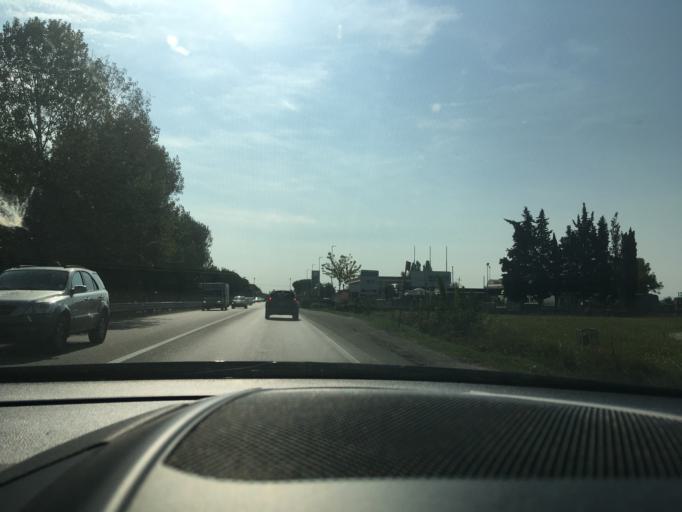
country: IT
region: Emilia-Romagna
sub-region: Provincia di Rimini
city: Santa Giustina
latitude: 44.1058
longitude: 12.4869
